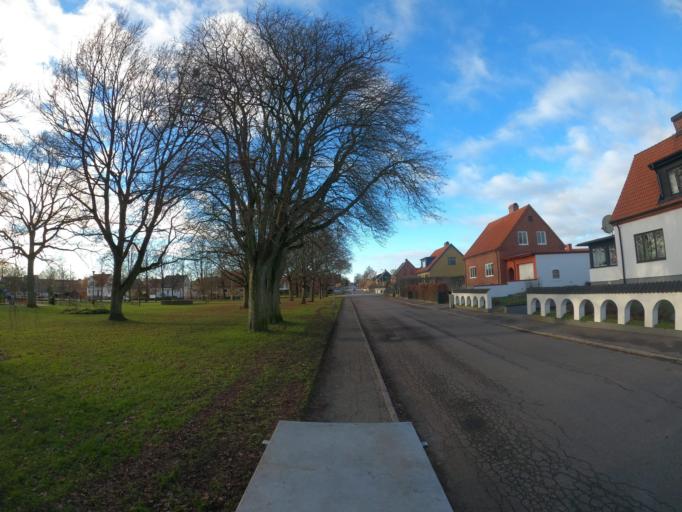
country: SE
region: Skane
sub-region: Svedala Kommun
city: Svedala
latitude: 55.5126
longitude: 13.2412
